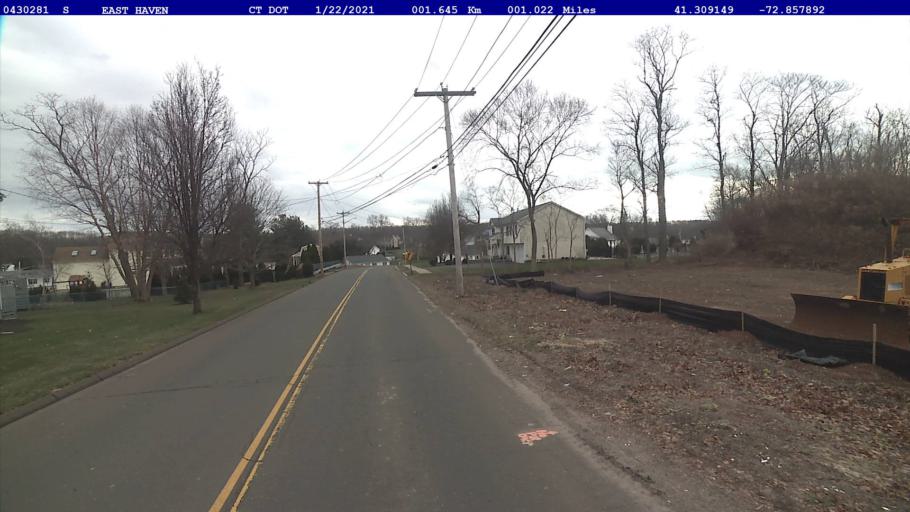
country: US
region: Connecticut
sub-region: New Haven County
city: East Haven
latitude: 41.3092
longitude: -72.8579
